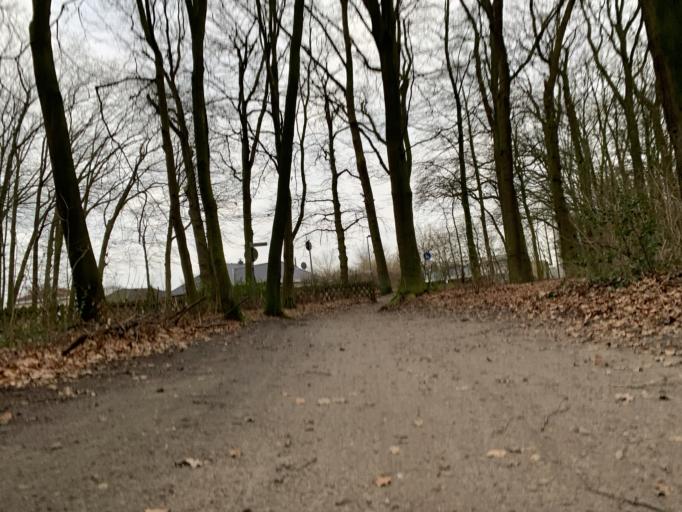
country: DE
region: Lower Saxony
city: Sulingen
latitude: 52.6803
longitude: 8.8174
